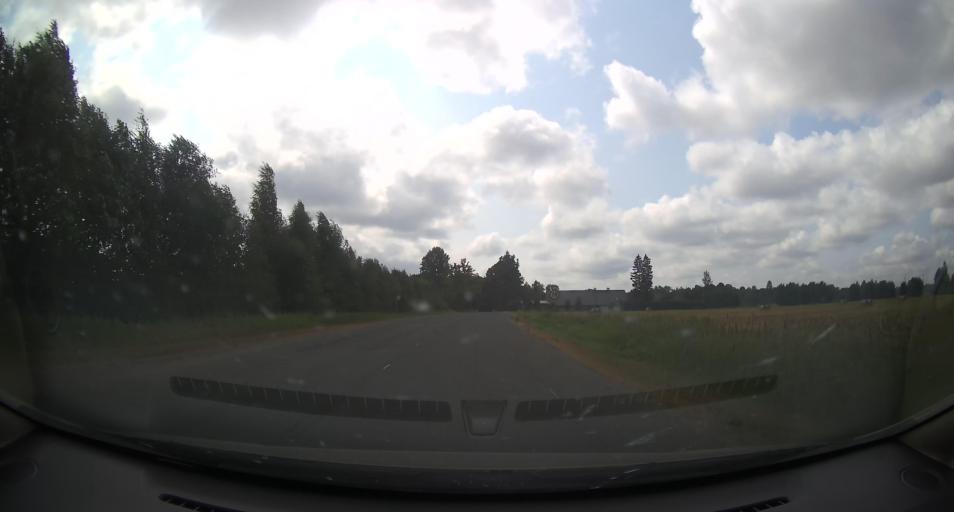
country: EE
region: Paernumaa
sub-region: Audru vald
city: Audru
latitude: 58.4477
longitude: 24.3113
